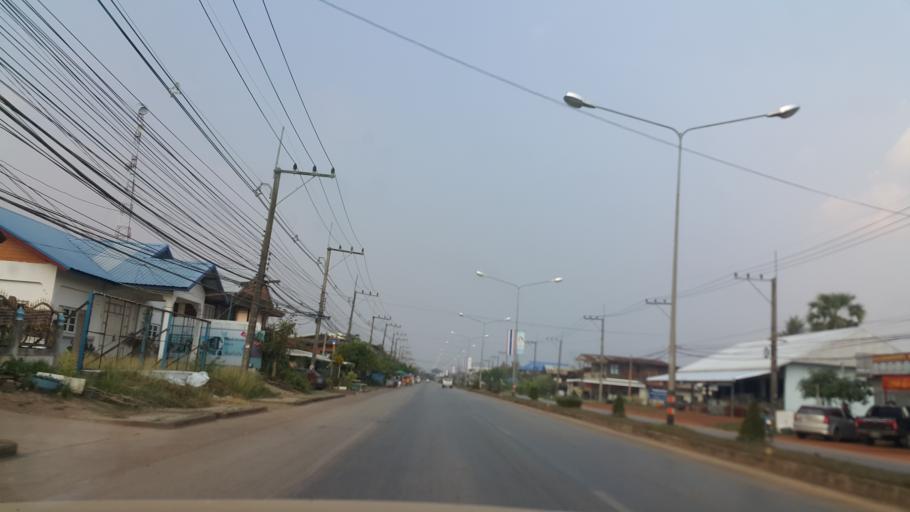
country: TH
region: Nakhon Phanom
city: That Phanom
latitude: 16.9619
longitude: 104.7262
